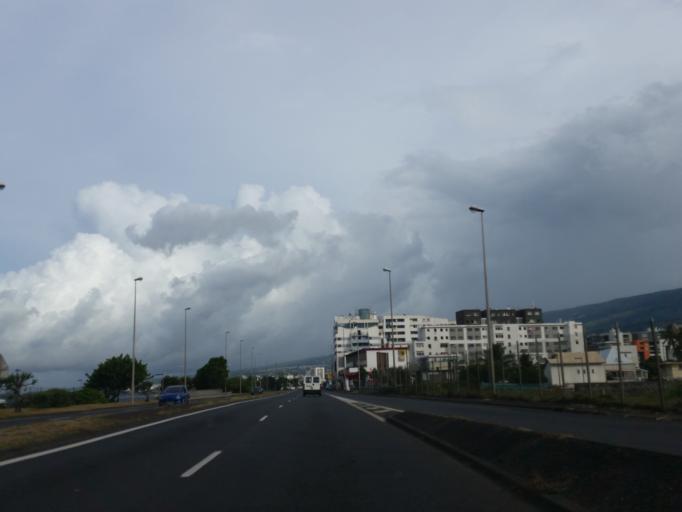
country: RE
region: Reunion
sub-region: Reunion
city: Saint-Denis
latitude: -20.8782
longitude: 55.4572
